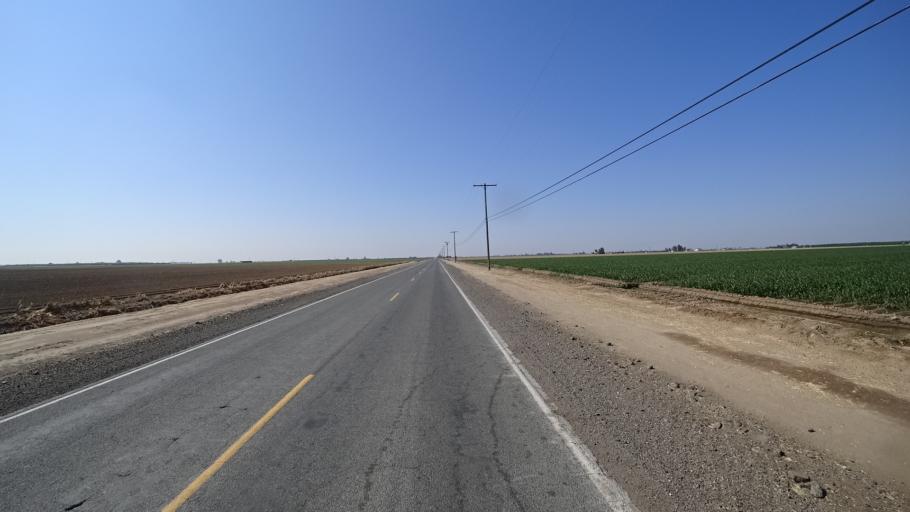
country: US
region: California
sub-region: Kings County
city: Hanford
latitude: 36.3667
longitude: -119.5650
